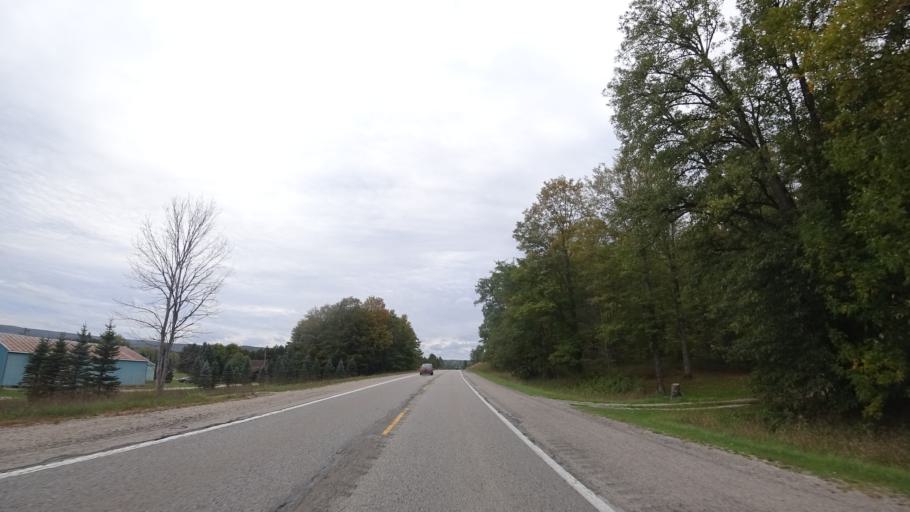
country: US
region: Michigan
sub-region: Charlevoix County
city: Boyne City
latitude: 45.1895
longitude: -84.9151
